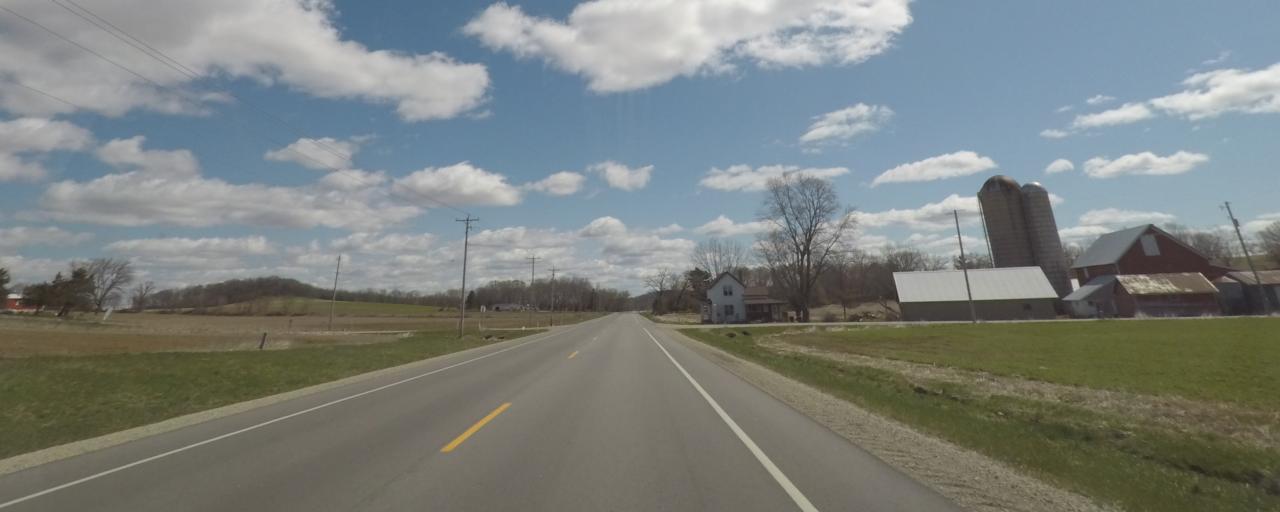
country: US
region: Wisconsin
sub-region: Jefferson County
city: Lake Mills
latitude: 43.0869
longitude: -88.9838
